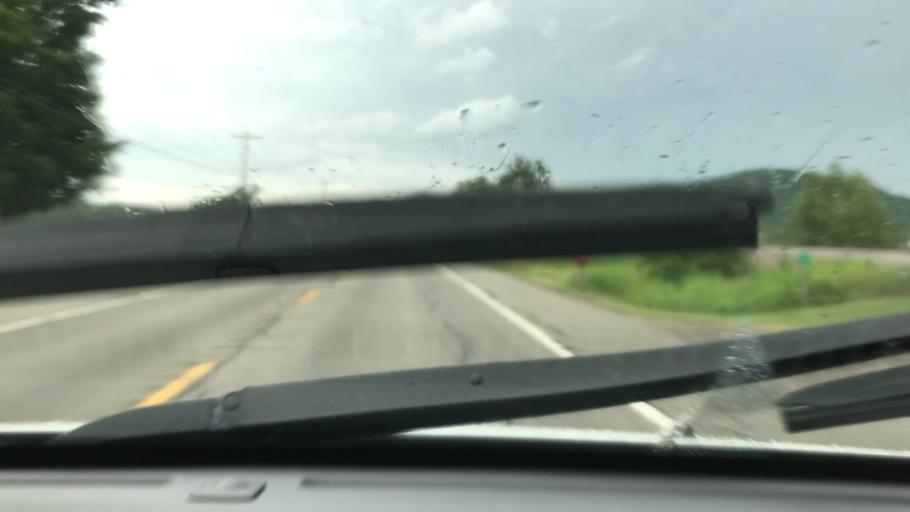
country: US
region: New York
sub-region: Cattaraugus County
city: Salamanca
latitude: 42.2450
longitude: -78.6436
